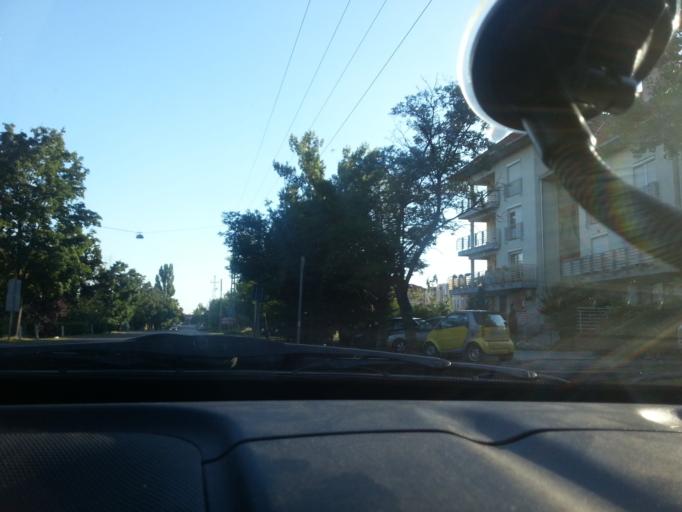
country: HU
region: Pest
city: Gyal
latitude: 47.4220
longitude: 19.2113
